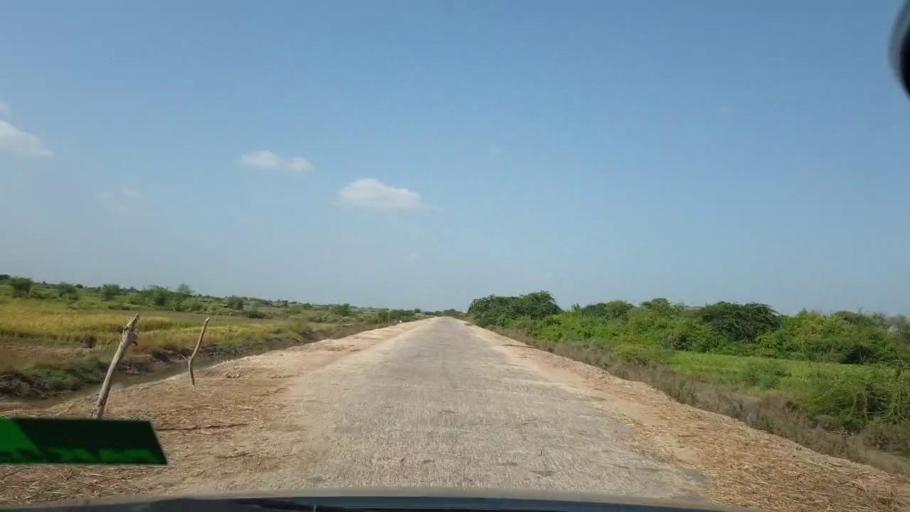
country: PK
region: Sindh
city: Tando Bago
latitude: 24.6903
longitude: 69.1887
